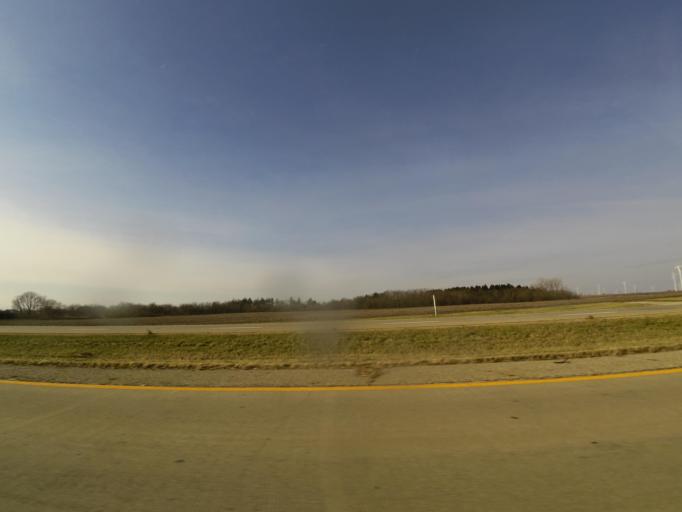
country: US
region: Illinois
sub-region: Macon County
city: Forsyth
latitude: 39.9622
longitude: -88.9559
